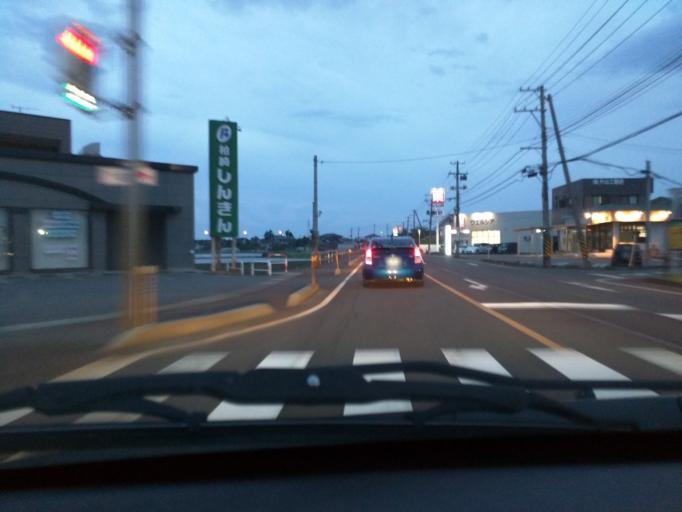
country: JP
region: Niigata
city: Kashiwazaki
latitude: 37.3557
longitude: 138.5971
